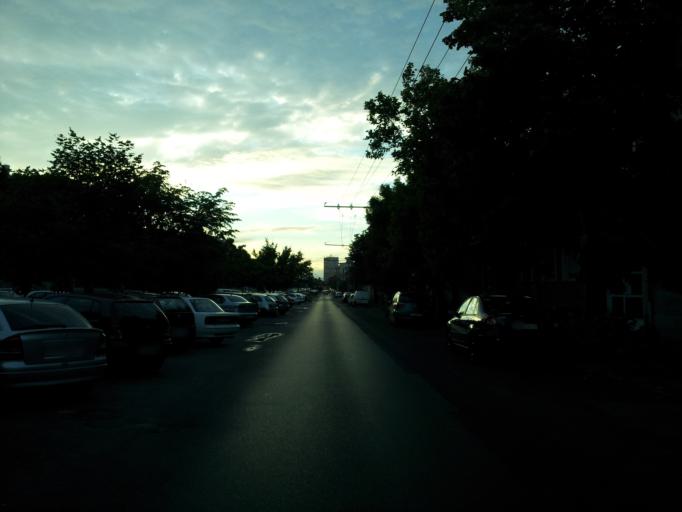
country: HU
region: Budapest
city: Budapest XIV. keruelet
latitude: 47.5180
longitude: 19.1061
